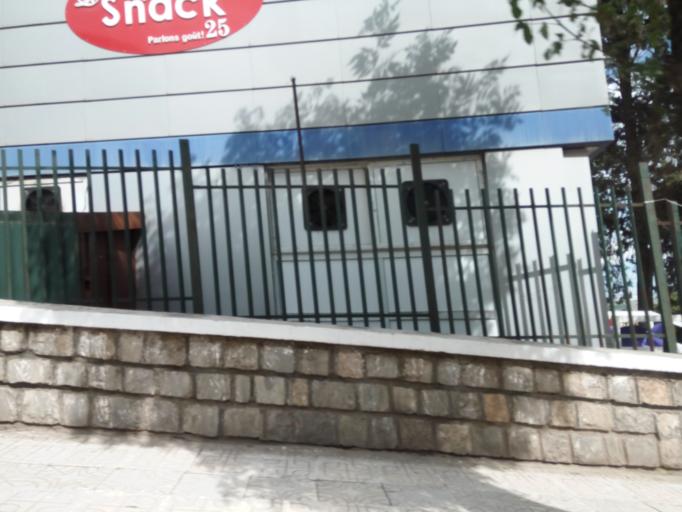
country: DZ
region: Constantine
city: Constantine
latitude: 36.3550
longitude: 6.6095
